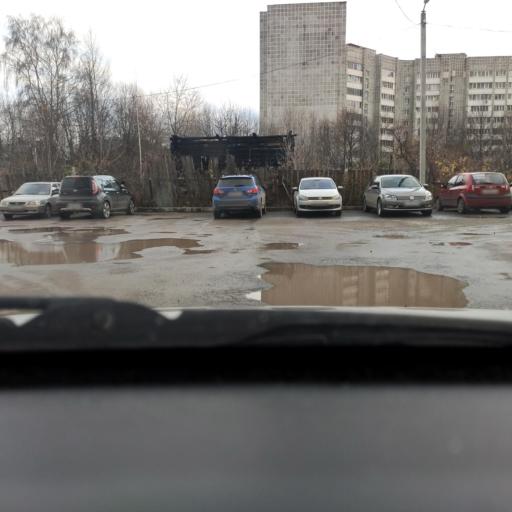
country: RU
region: Perm
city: Perm
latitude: 58.0296
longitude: 56.3270
